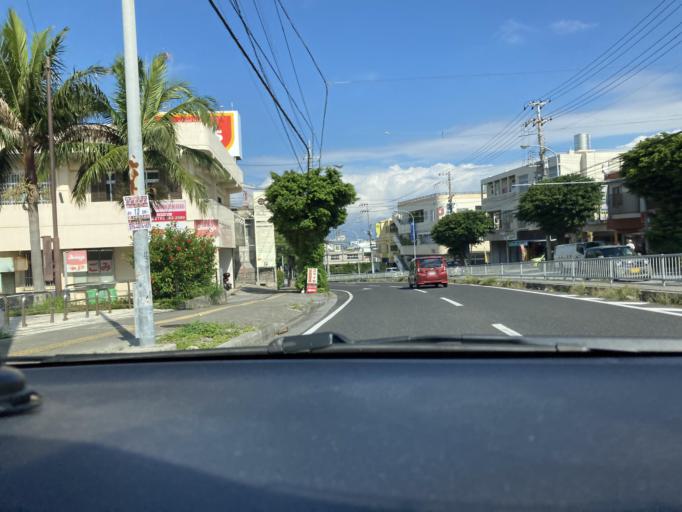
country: JP
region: Okinawa
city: Naha-shi
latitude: 26.2374
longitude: 127.6965
